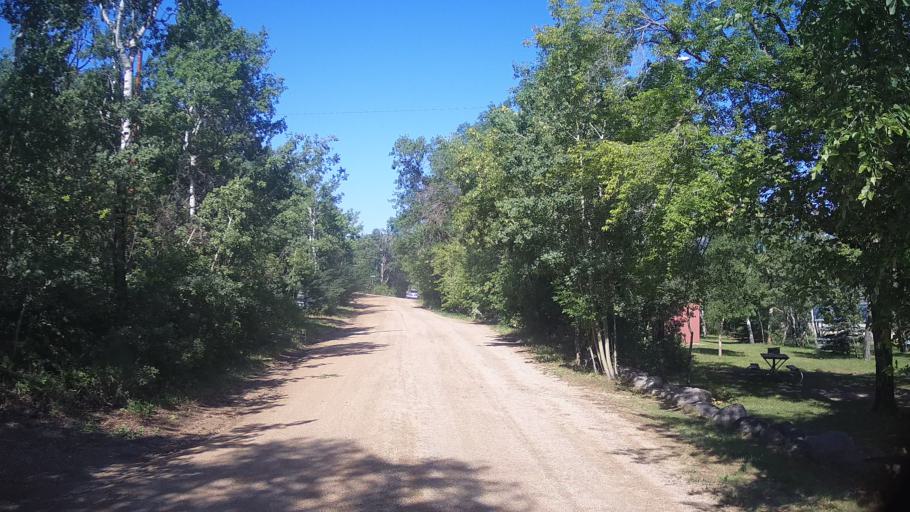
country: CA
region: Saskatchewan
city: Watrous
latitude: 51.7216
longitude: -105.4526
